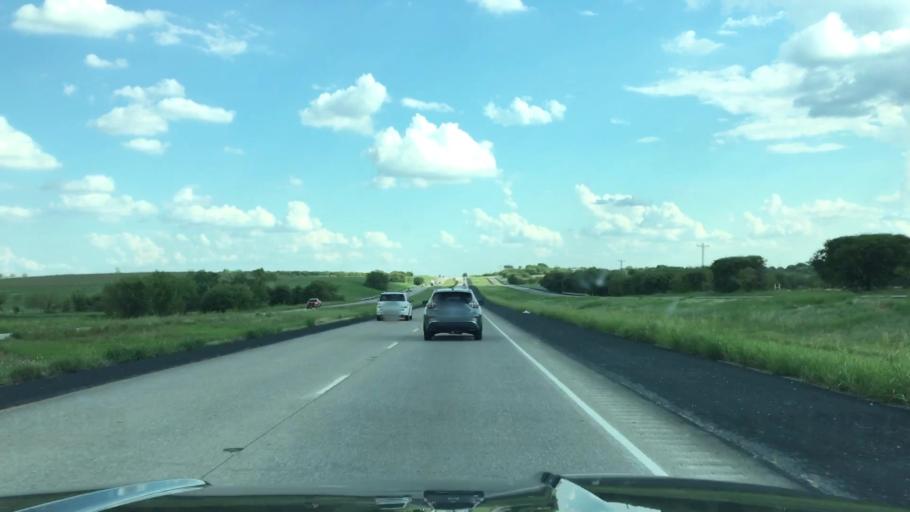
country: US
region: Texas
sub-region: Wise County
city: Newark
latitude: 33.0013
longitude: -97.4346
